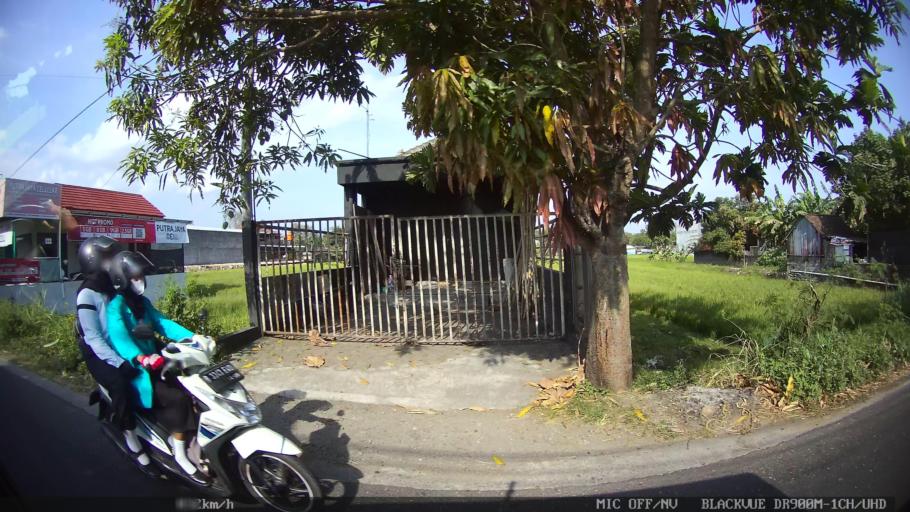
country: ID
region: Daerah Istimewa Yogyakarta
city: Kasihan
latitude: -7.8453
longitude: 110.3432
